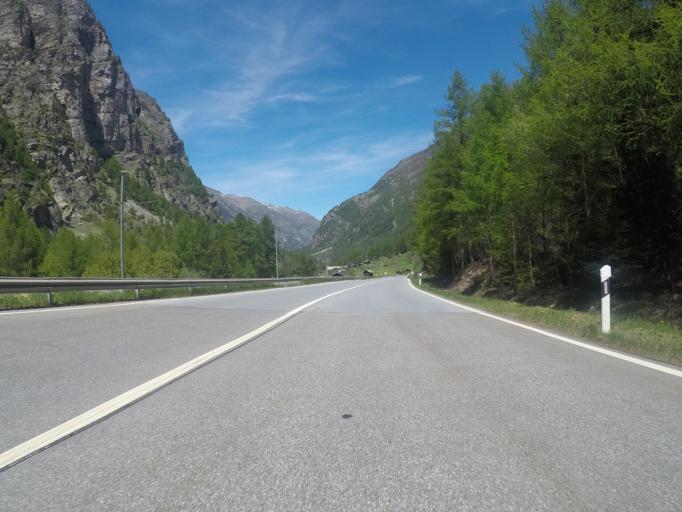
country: CH
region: Valais
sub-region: Visp District
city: Sankt Niklaus
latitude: 46.1158
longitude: 7.7865
